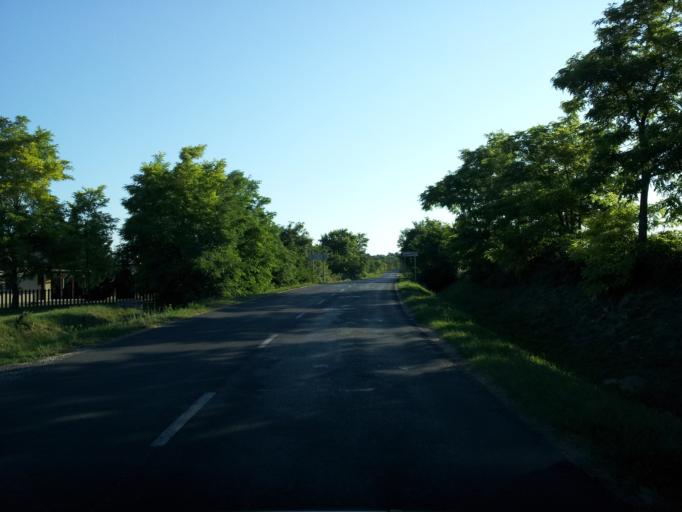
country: HU
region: Fejer
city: Lepseny
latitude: 47.0260
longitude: 18.2136
